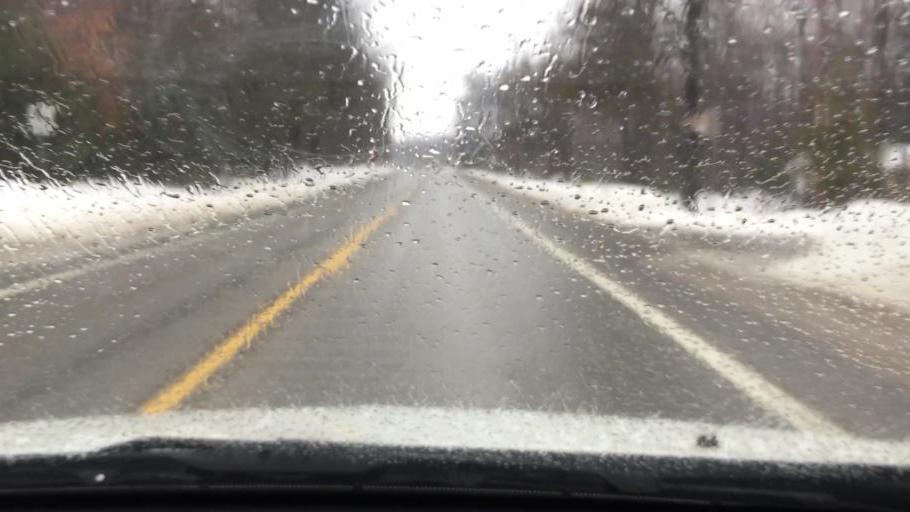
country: US
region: Michigan
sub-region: Charlevoix County
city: East Jordan
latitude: 45.2005
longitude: -85.1651
